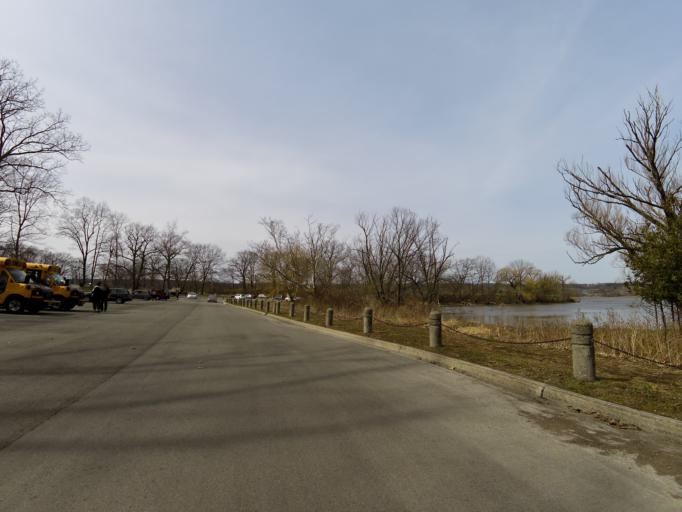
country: CA
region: Ontario
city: Hamilton
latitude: 43.2734
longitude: -79.8957
